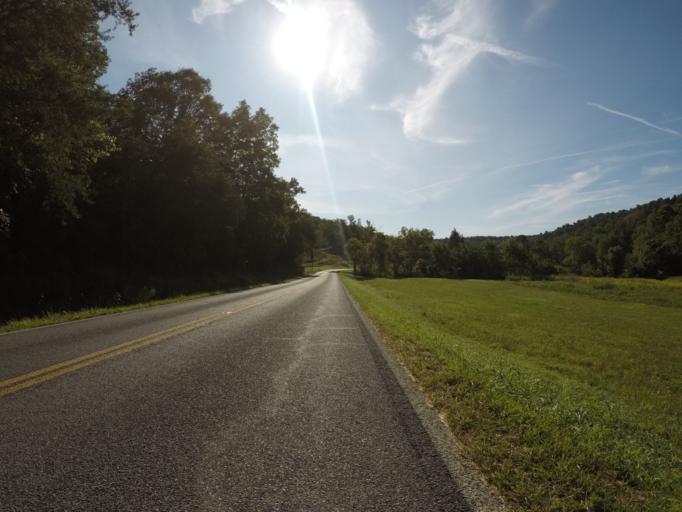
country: US
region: Ohio
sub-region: Lawrence County
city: Burlington
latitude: 38.4985
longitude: -82.5065
